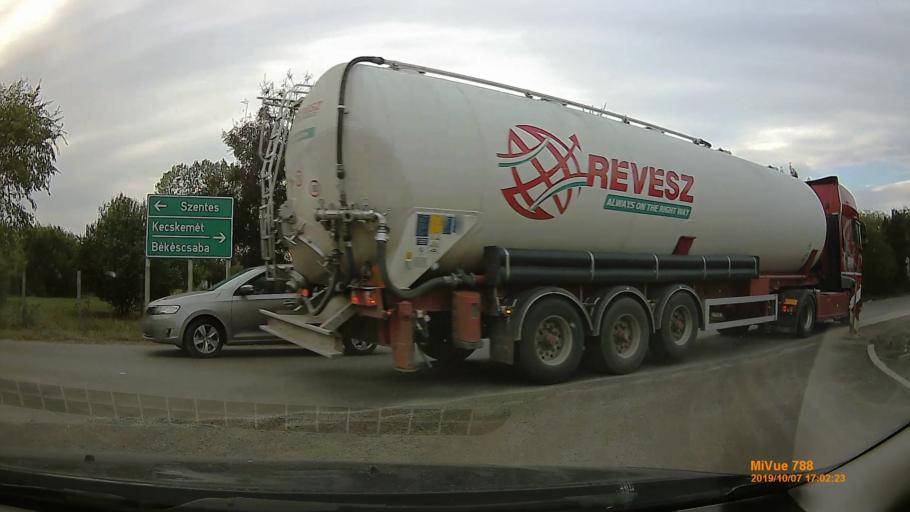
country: HU
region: Bekes
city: Szarvas
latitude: 46.8522
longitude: 20.5573
